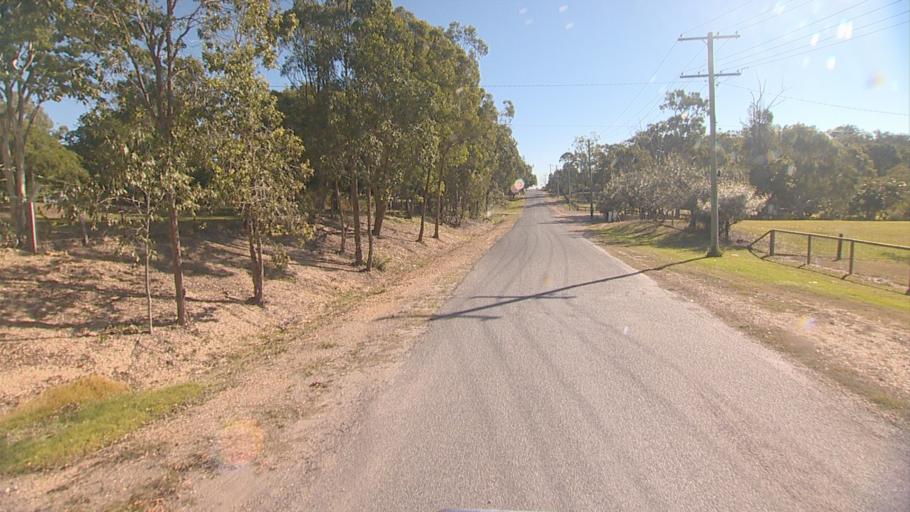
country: AU
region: Queensland
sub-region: Logan
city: Logan Reserve
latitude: -27.7430
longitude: 153.1377
